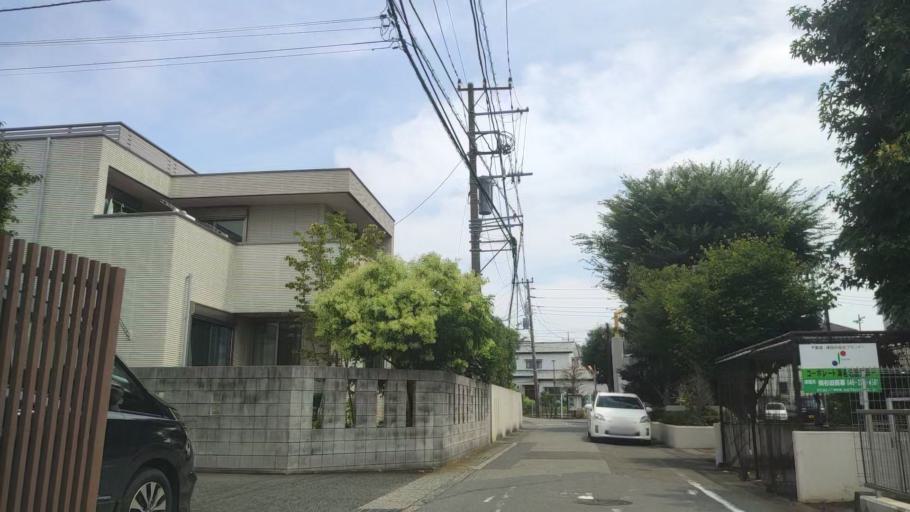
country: JP
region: Kanagawa
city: Zama
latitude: 35.4613
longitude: 139.3960
